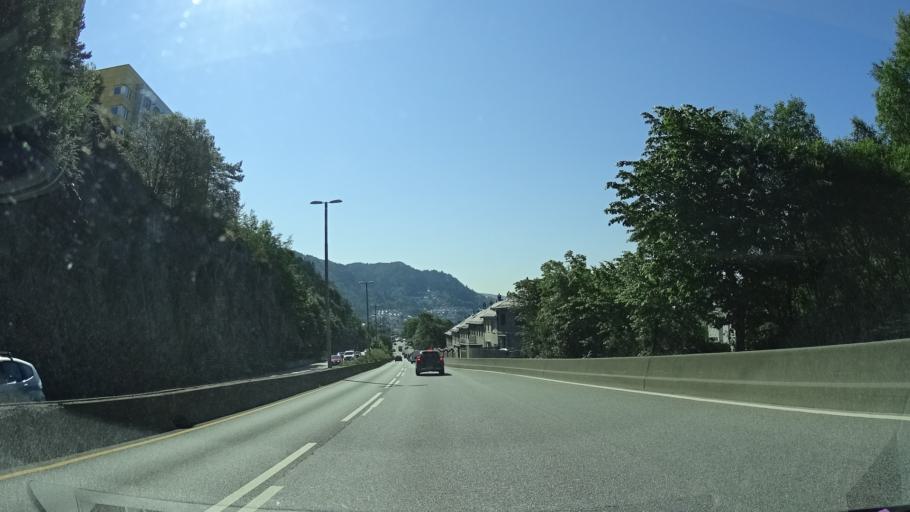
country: NO
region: Hordaland
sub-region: Bergen
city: Bergen
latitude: 60.4229
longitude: 5.3056
